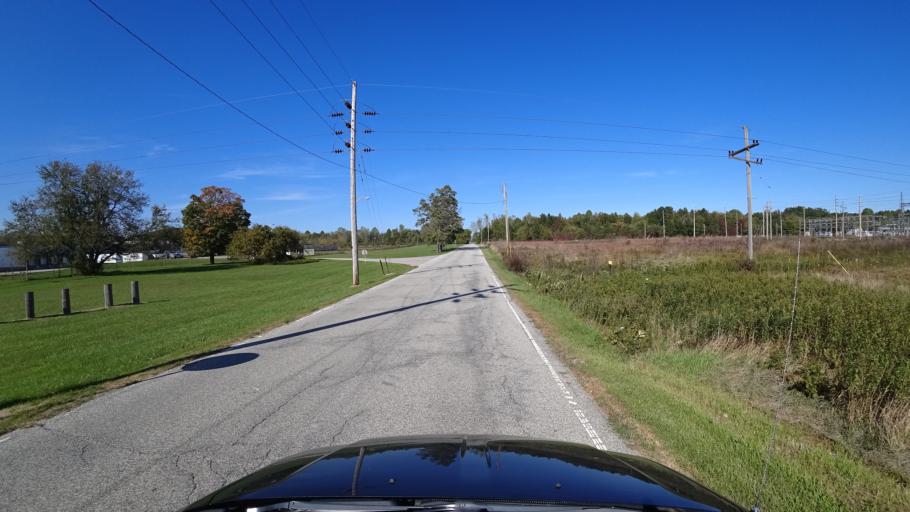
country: US
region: Indiana
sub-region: LaPorte County
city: Trail Creek
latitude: 41.7118
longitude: -86.8405
